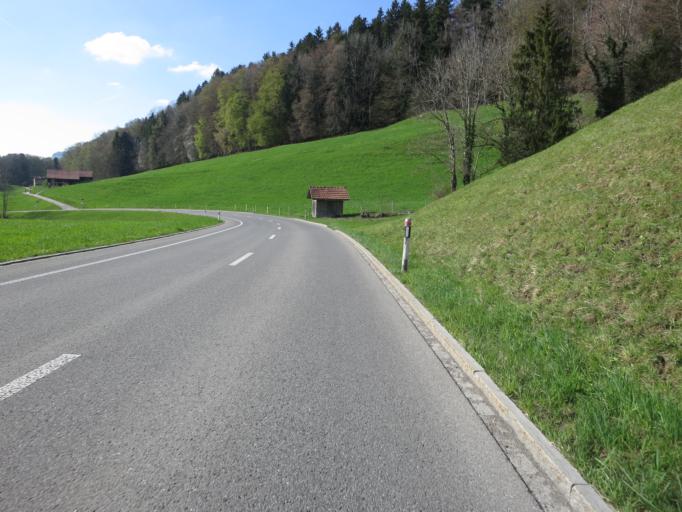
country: CH
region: Saint Gallen
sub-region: Wahlkreis See-Gaster
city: Goldingen
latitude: 47.2656
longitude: 8.9473
